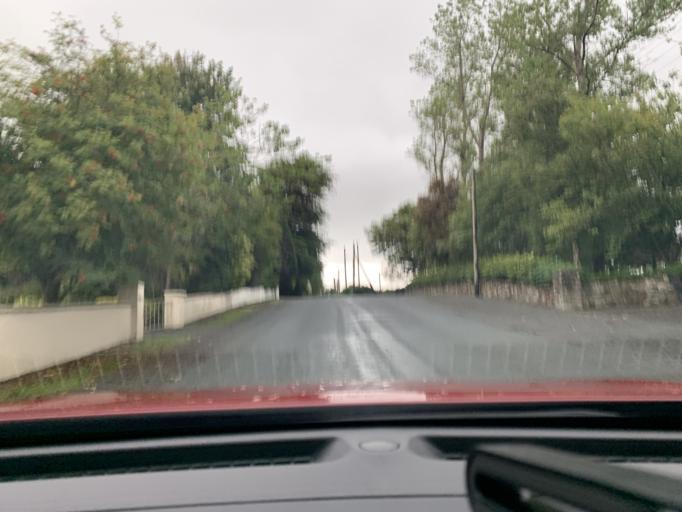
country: IE
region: Connaught
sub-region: Sligo
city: Sligo
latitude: 54.3032
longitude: -8.5136
